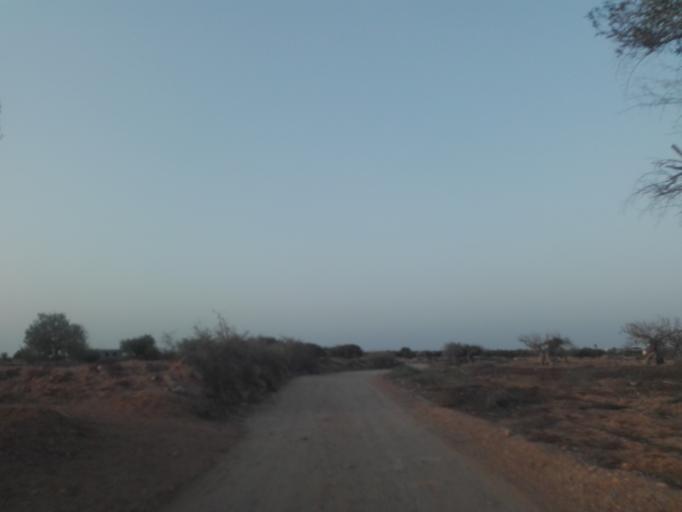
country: TN
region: Madanin
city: Houmt Souk
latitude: 33.7375
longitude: 10.7630
